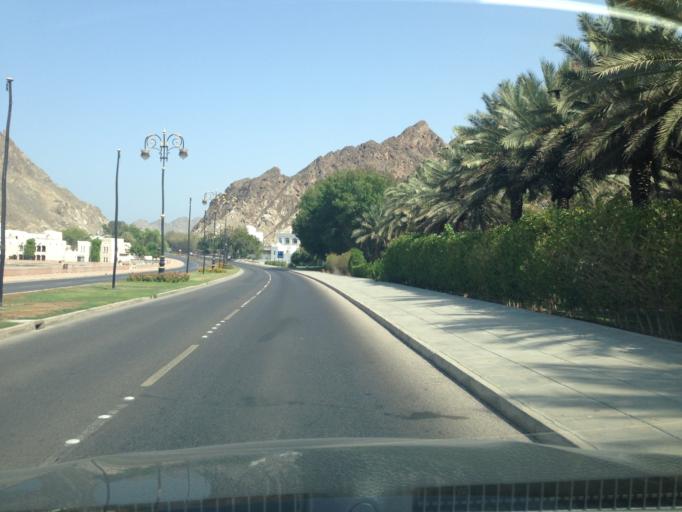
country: OM
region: Muhafazat Masqat
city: Muscat
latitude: 23.6220
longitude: 58.5822
